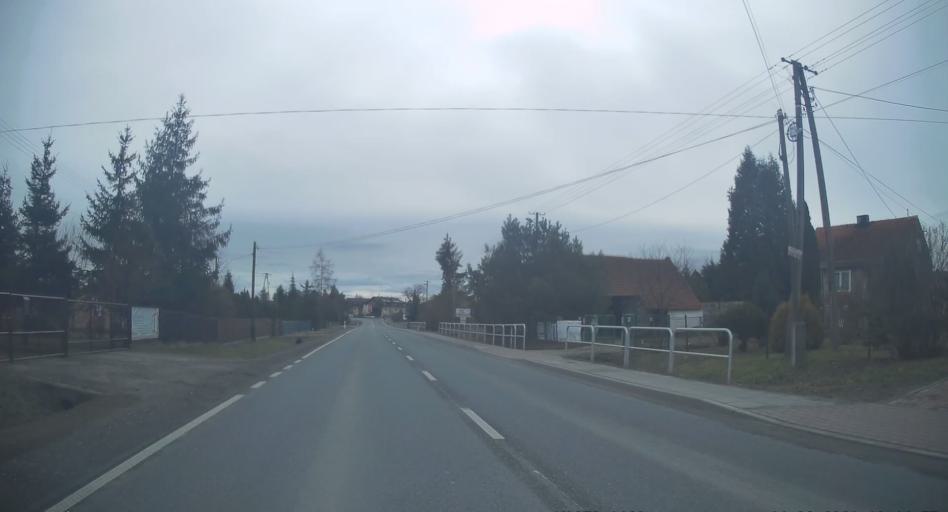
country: PL
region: Lesser Poland Voivodeship
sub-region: Powiat wielicki
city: Szarow
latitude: 50.0028
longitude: 20.2678
